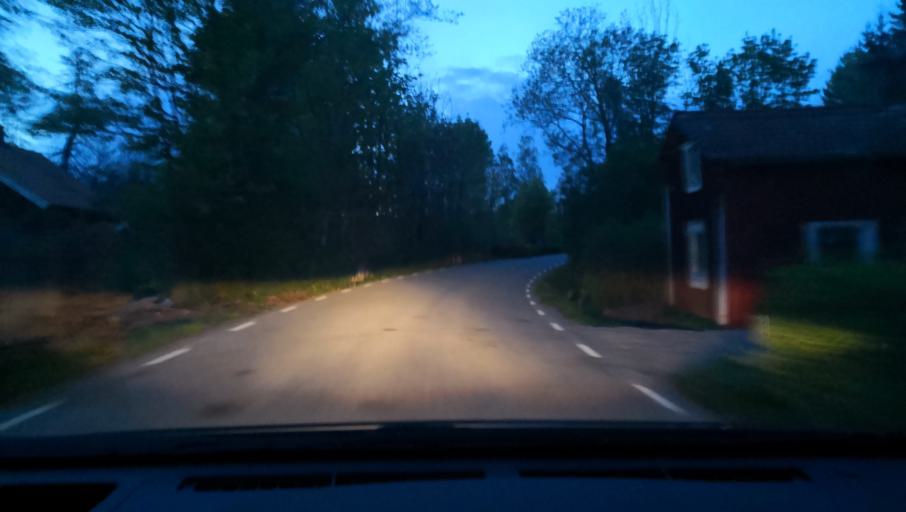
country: SE
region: OErebro
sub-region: Orebro Kommun
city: Vintrosa
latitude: 59.1752
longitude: 15.0170
